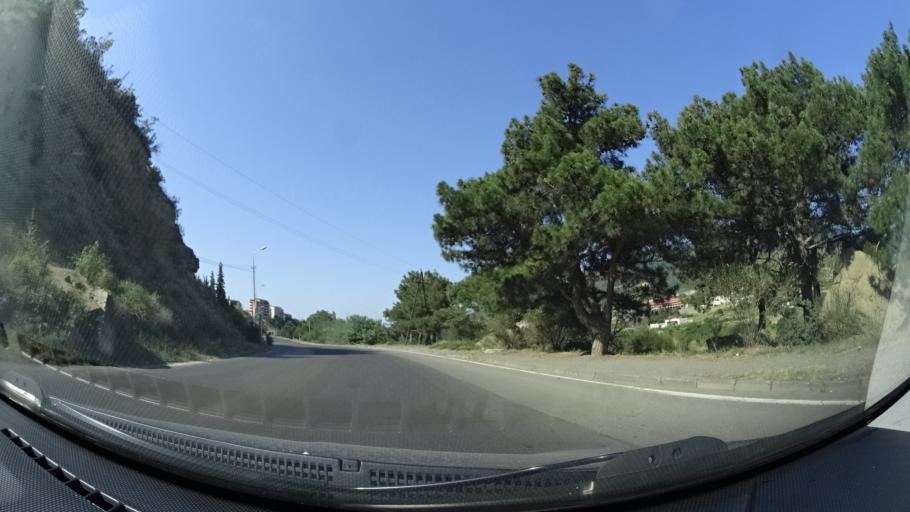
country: GE
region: Mtskheta-Mtianeti
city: Mtskheta
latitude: 41.8565
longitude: 44.7227
